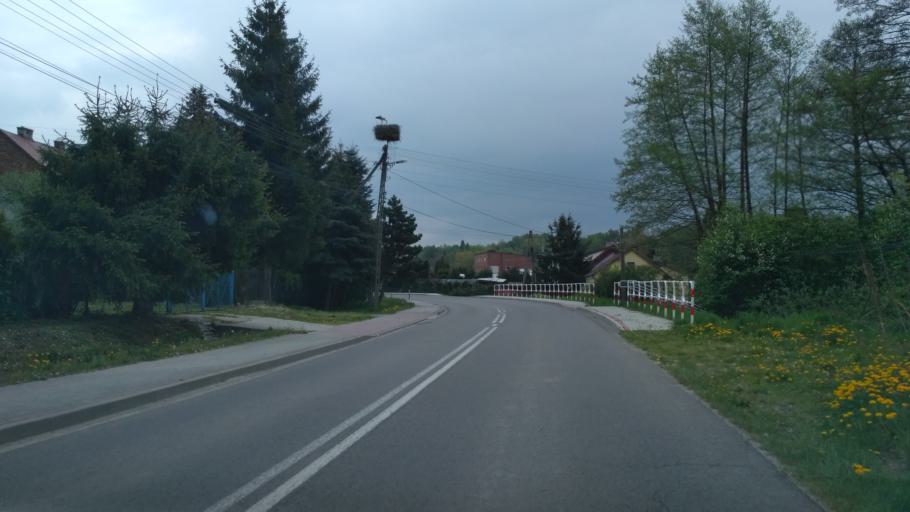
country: PL
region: Lesser Poland Voivodeship
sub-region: Powiat tarnowski
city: Skrzyszow
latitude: 49.9873
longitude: 21.0864
